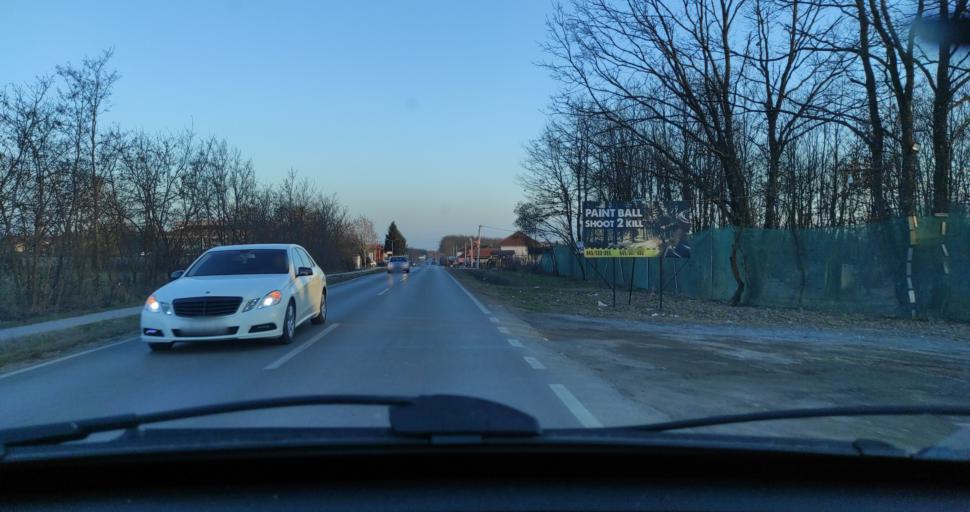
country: XK
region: Gjakova
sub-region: Komuna e Decanit
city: Gllogjan
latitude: 42.4616
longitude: 20.3496
